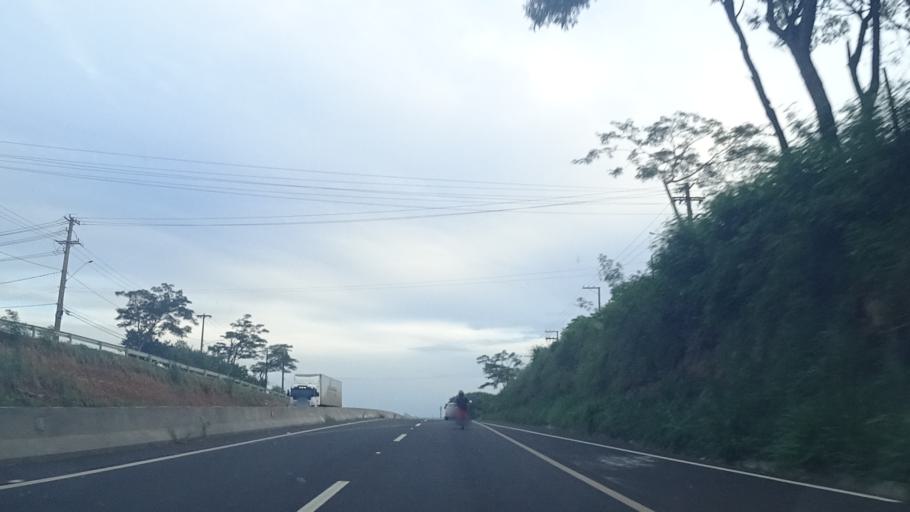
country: BR
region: Sao Paulo
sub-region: Presidente Prudente
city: Presidente Prudente
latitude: -22.1588
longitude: -51.3942
